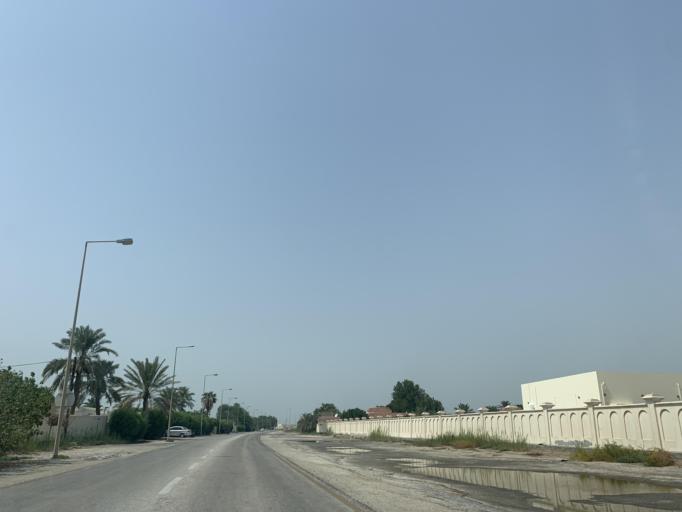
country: BH
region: Central Governorate
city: Madinat Hamad
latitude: 26.1628
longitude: 50.4656
